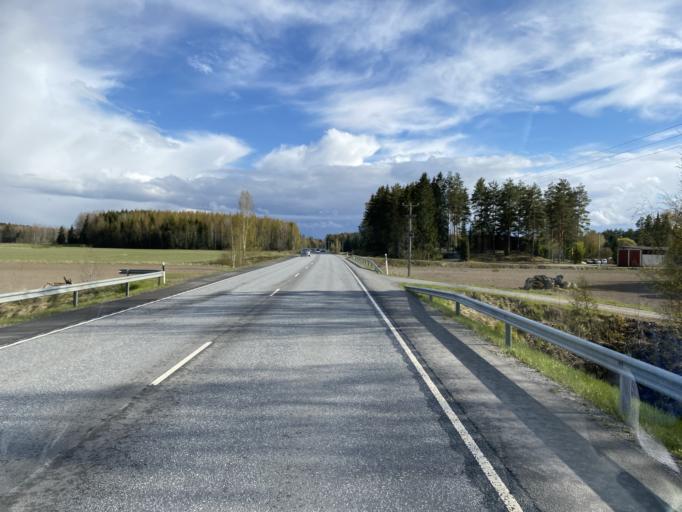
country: FI
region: Pirkanmaa
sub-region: Tampere
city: Lempaeaelae
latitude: 61.2823
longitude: 23.7441
